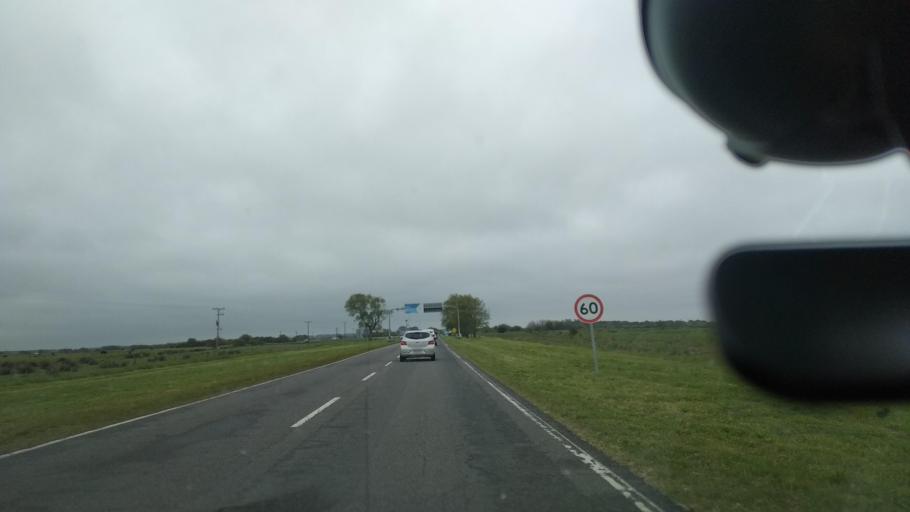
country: AR
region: Buenos Aires
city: Veronica
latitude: -35.5964
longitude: -57.2713
